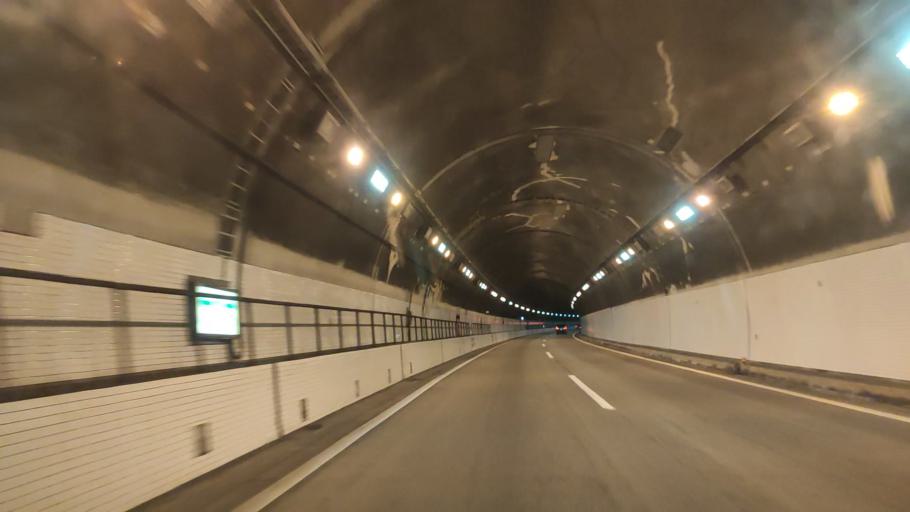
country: JP
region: Ehime
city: Niihama
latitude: 33.9169
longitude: 133.3105
